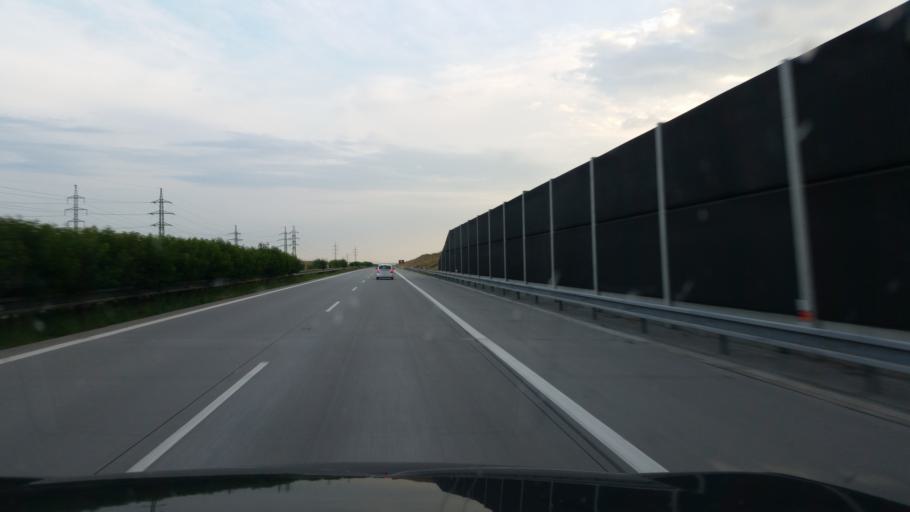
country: CZ
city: Jesenik nad Odrou
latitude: 49.6602
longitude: 17.9047
